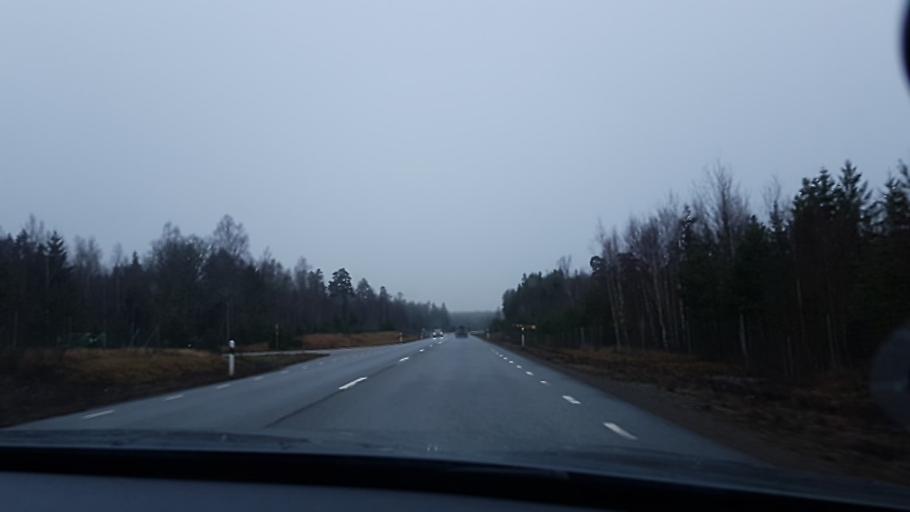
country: SE
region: Vaestra Goetaland
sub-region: Gullspangs Kommun
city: Gullspang
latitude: 58.8639
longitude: 14.0070
